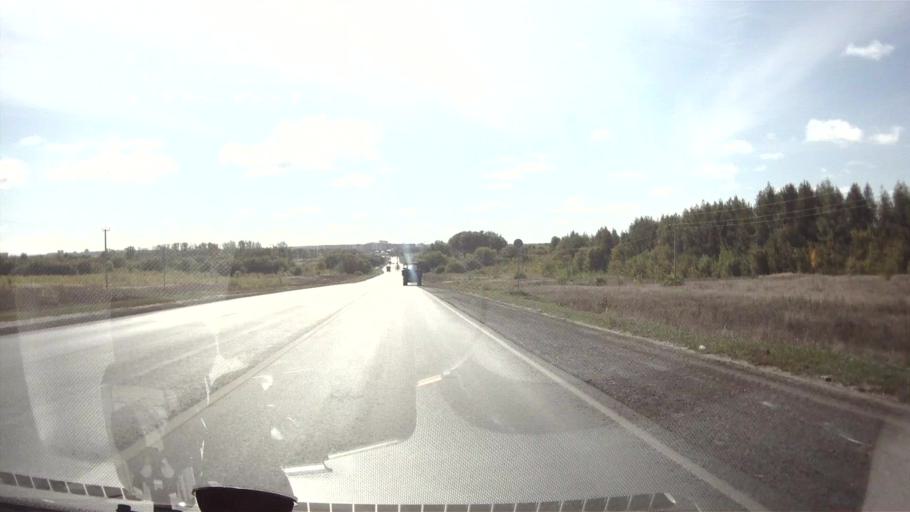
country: RU
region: Ulyanovsk
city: Isheyevka
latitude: 54.3083
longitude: 48.2385
